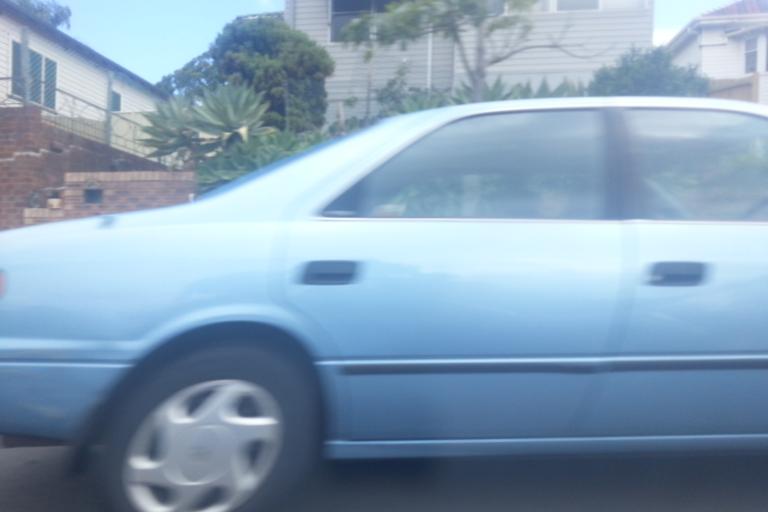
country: AU
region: New South Wales
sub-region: Wollongong
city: Wollongong
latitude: -34.4284
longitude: 150.8821
